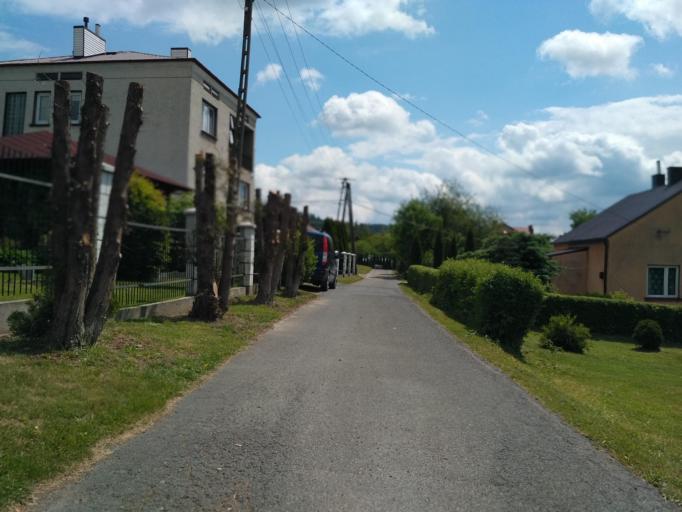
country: PL
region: Subcarpathian Voivodeship
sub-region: Powiat strzyzowski
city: Czudec
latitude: 49.9456
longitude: 21.8432
